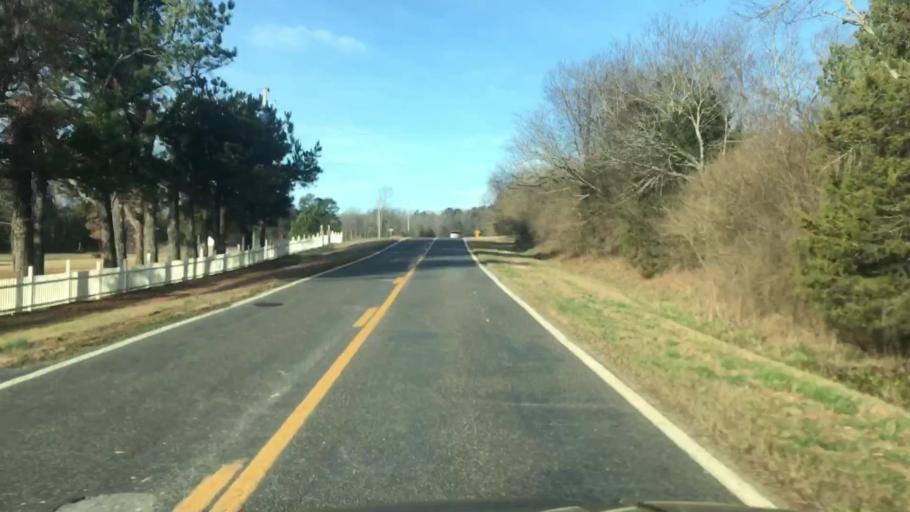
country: US
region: Arkansas
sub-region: Garland County
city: Rockwell
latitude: 34.4713
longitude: -93.2520
